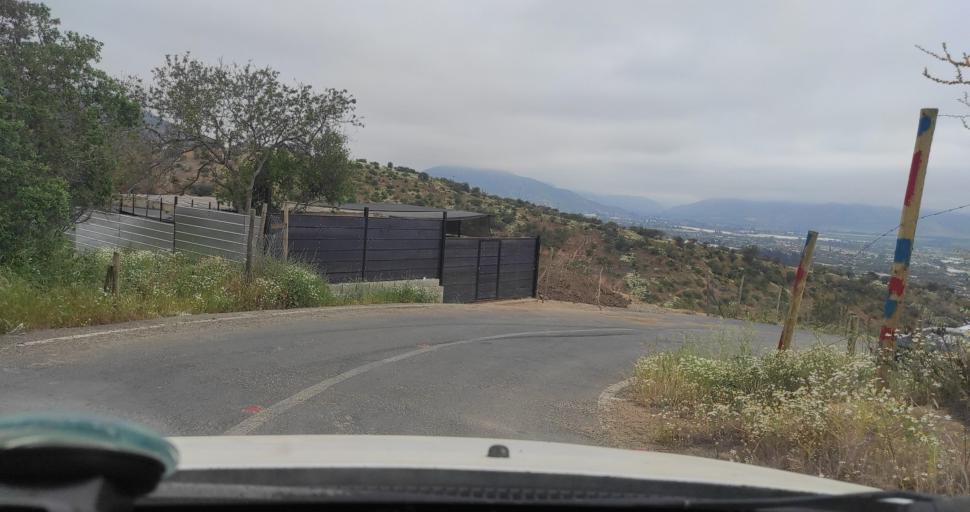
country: CL
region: Valparaiso
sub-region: Provincia de Marga Marga
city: Limache
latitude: -32.9832
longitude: -71.2247
